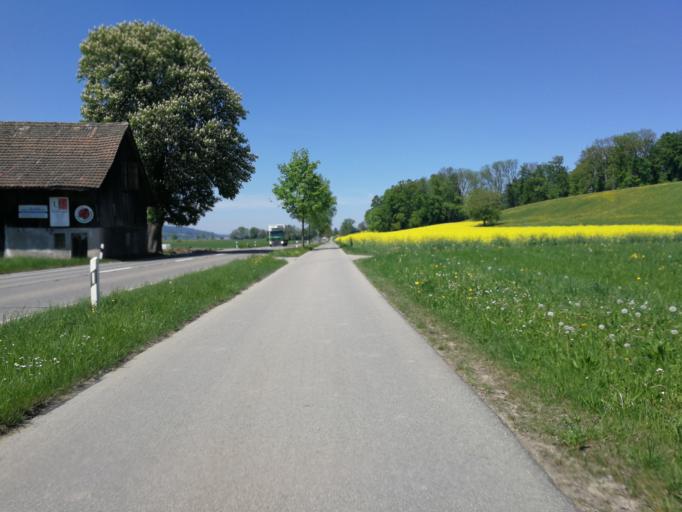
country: CH
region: Zurich
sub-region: Bezirk Uster
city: Monchaltorf
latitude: 47.3190
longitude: 8.7176
